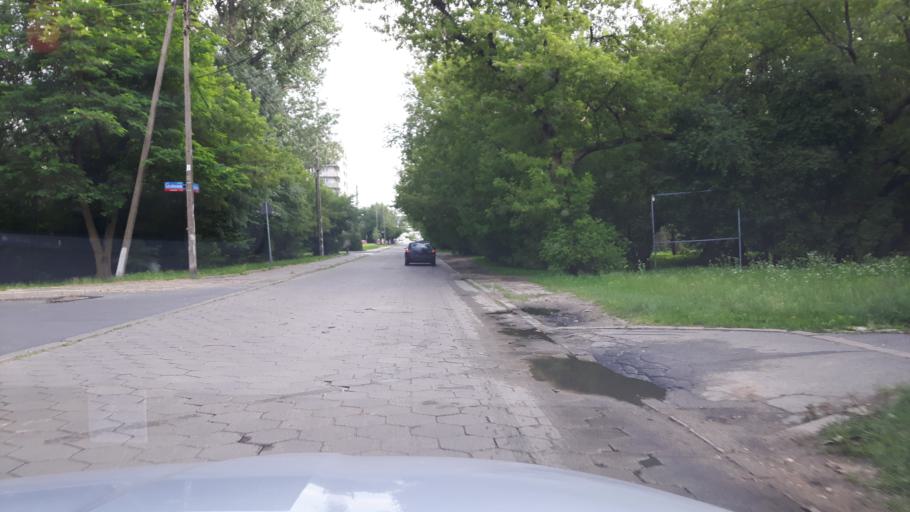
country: PL
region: Masovian Voivodeship
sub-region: Warszawa
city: Praga Poludnie
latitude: 52.2424
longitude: 21.1146
